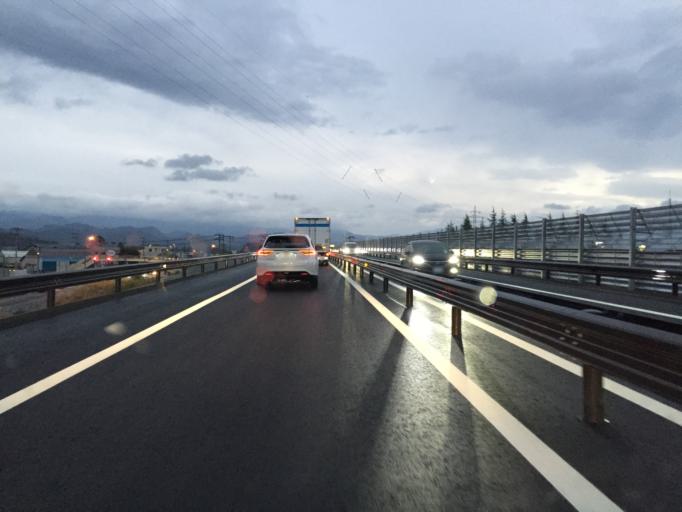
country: JP
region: Yamagata
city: Yonezawa
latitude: 37.9440
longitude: 140.1191
